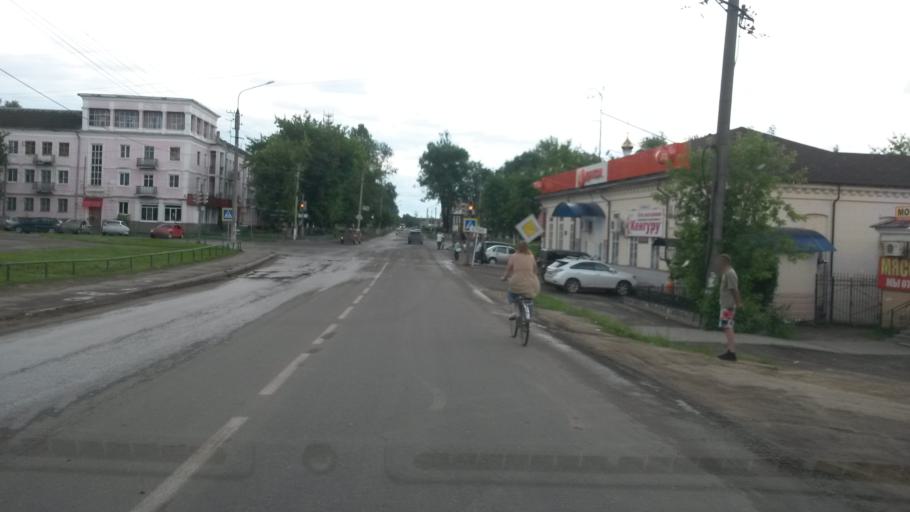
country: RU
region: Jaroslavl
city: Gavrilov-Yam
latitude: 57.3054
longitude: 39.8531
